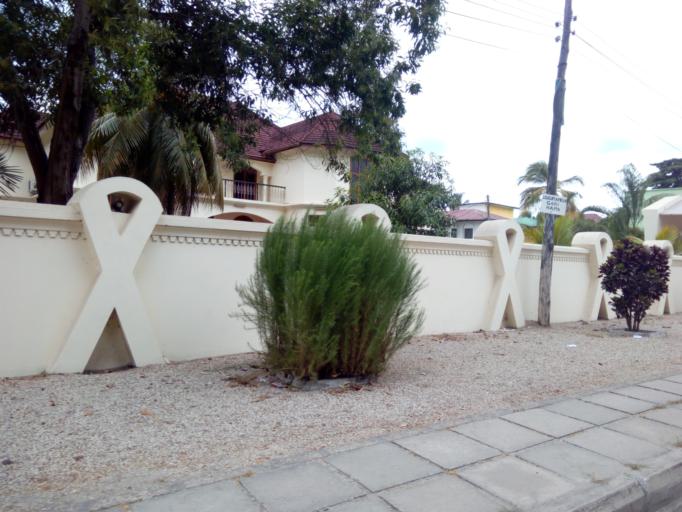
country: TZ
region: Zanzibar Urban/West
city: Zanzibar
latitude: -6.1833
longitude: 39.2055
